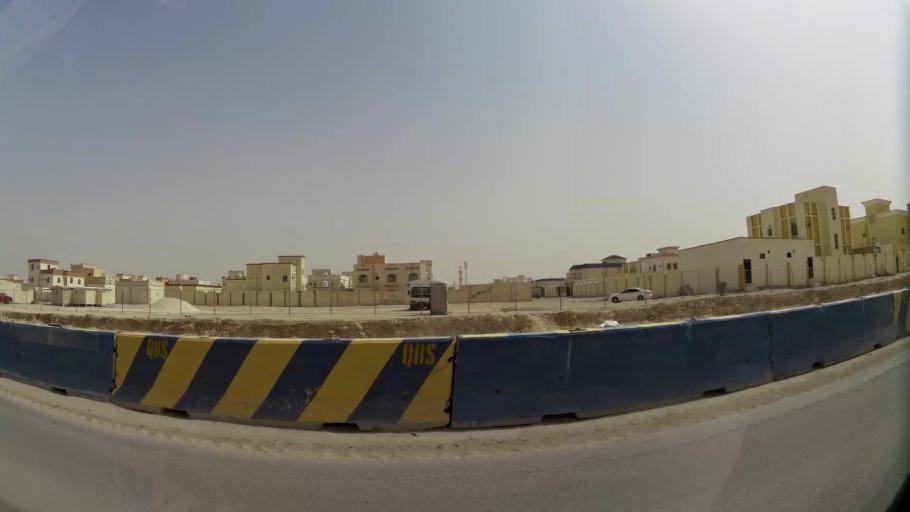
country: QA
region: Baladiyat ar Rayyan
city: Ar Rayyan
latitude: 25.2534
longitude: 51.3672
